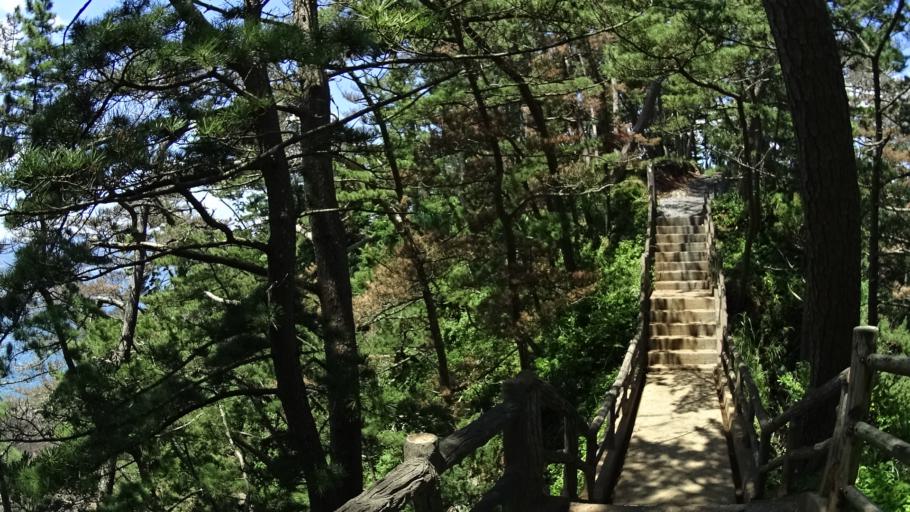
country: JP
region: Iwate
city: Ofunato
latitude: 38.8312
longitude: 141.6245
